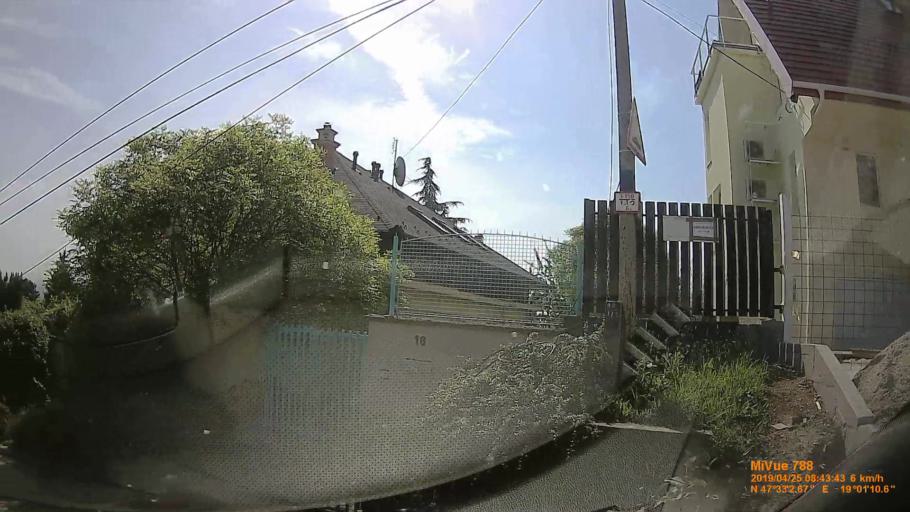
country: HU
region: Budapest
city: Budapest III. keruelet
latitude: 47.5507
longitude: 19.0197
